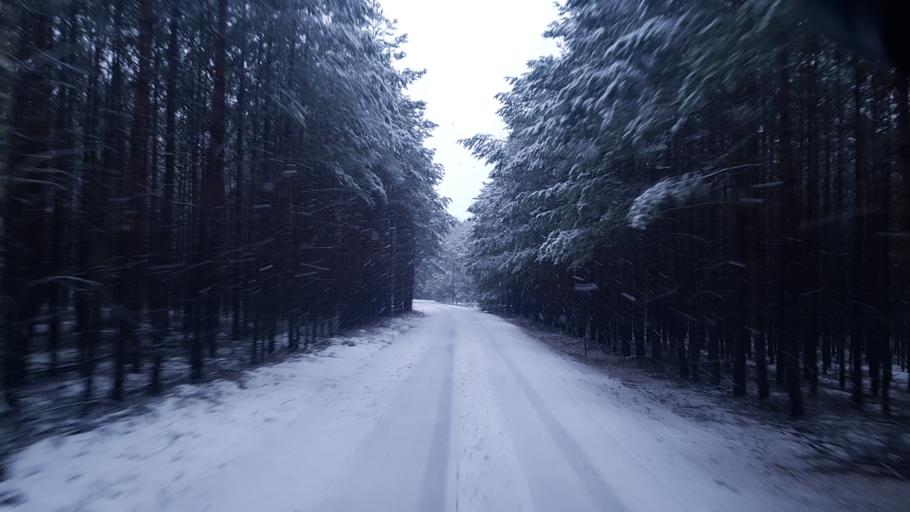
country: DE
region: Brandenburg
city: Janschwalde
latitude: 51.9074
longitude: 14.5466
